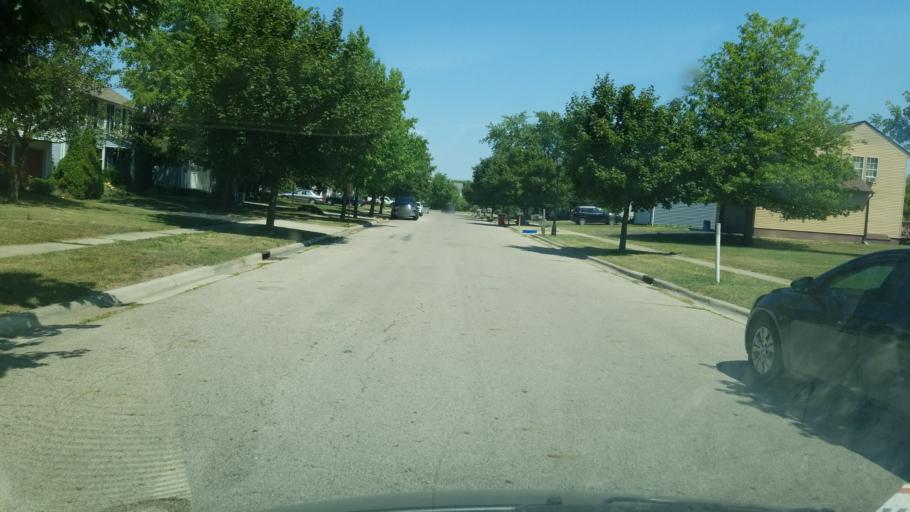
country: US
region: Ohio
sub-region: Franklin County
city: Grove City
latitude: 39.8920
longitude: -83.1104
